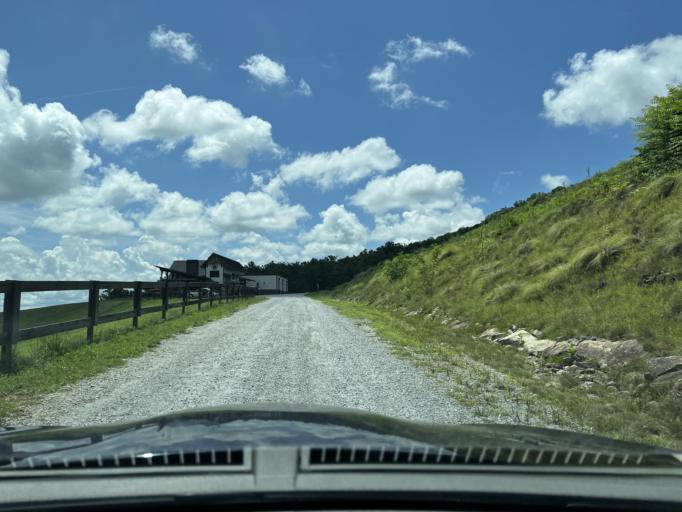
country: US
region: North Carolina
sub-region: Henderson County
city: Fruitland
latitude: 35.4104
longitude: -82.3953
